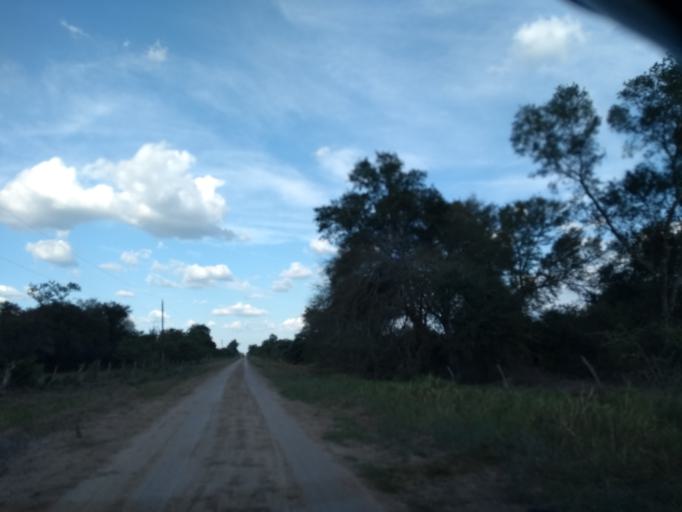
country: AR
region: Chaco
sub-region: Departamento de Quitilipi
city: Quitilipi
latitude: -26.7541
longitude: -60.2514
